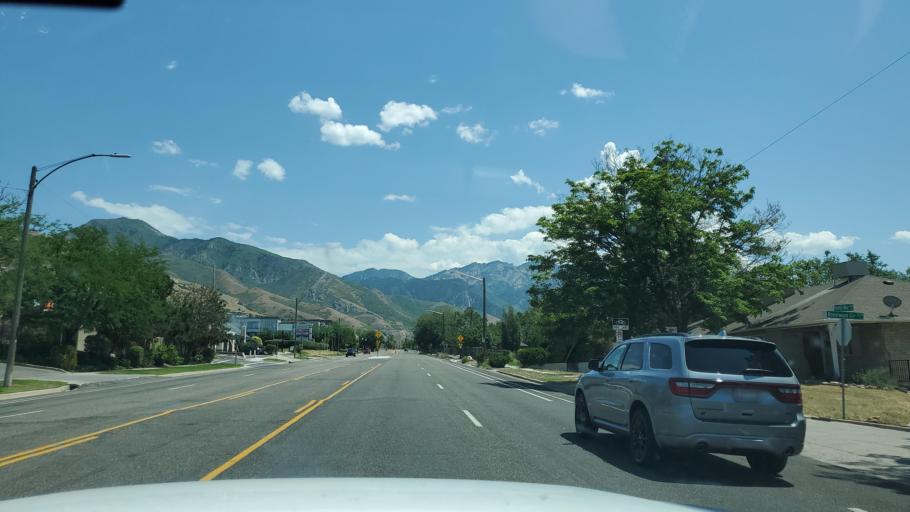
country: US
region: Utah
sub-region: Salt Lake County
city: Canyon Rim
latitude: 40.7214
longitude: -111.8184
